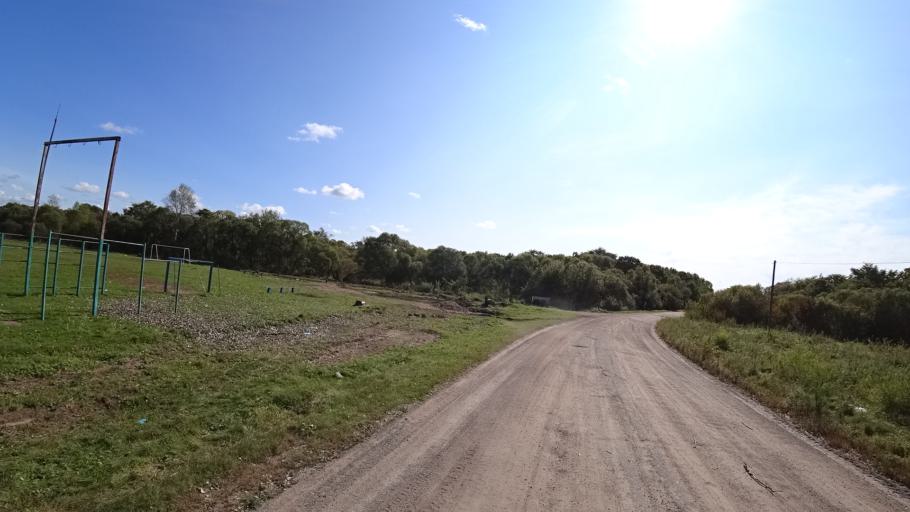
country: RU
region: Amur
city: Arkhara
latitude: 49.4011
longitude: 130.1380
